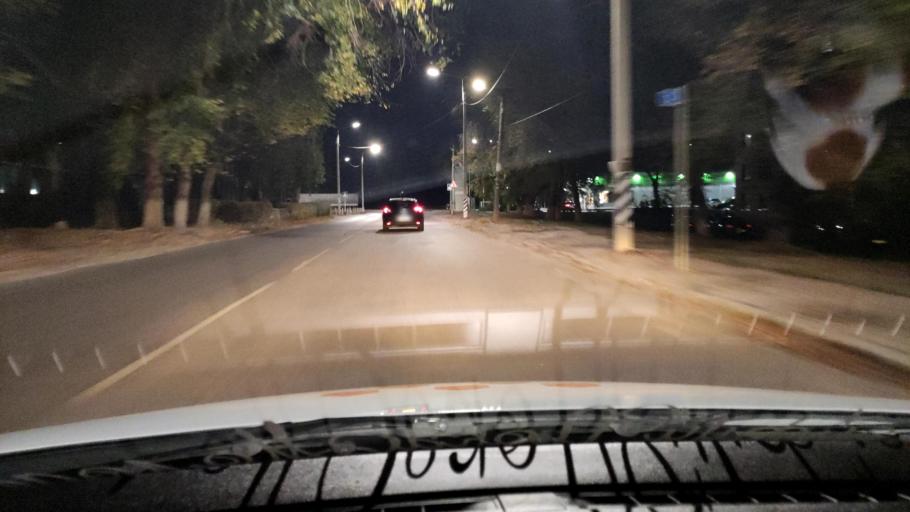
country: RU
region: Voronezj
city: Semiluki
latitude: 51.6785
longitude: 39.0301
